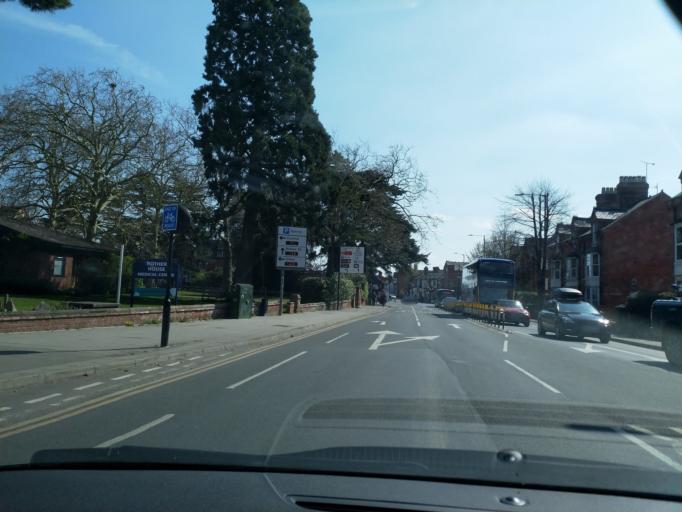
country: GB
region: England
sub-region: Warwickshire
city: Stratford-upon-Avon
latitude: 52.1935
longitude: -1.7143
